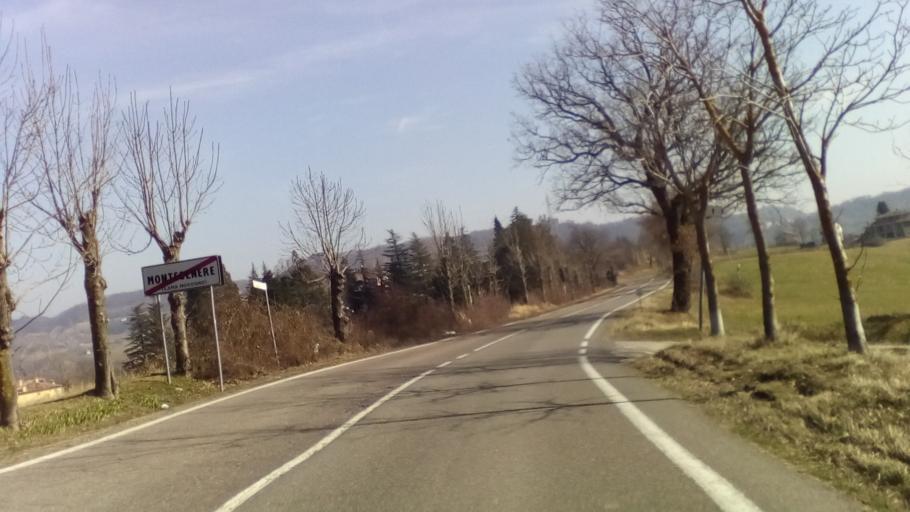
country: IT
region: Emilia-Romagna
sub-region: Provincia di Modena
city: Lama
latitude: 44.3117
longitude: 10.7814
